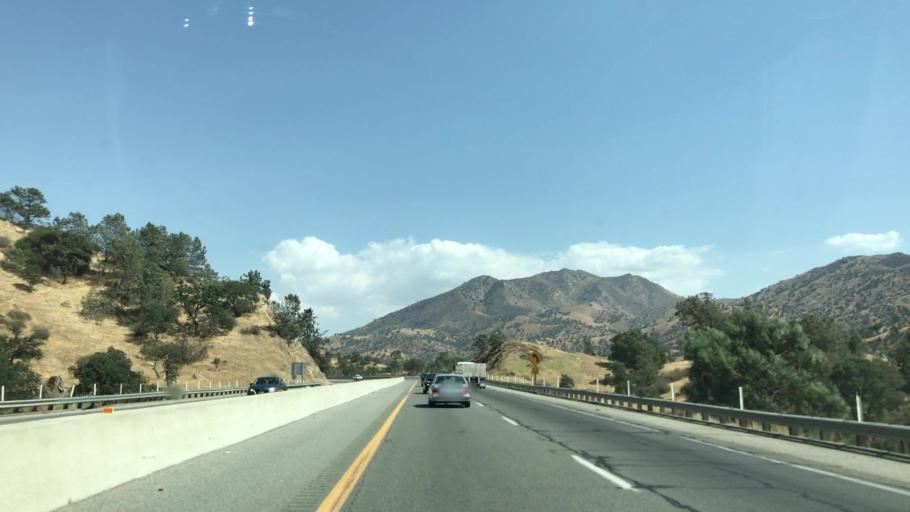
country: US
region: California
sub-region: Kern County
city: Bear Valley Springs
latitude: 35.2173
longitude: -118.5531
